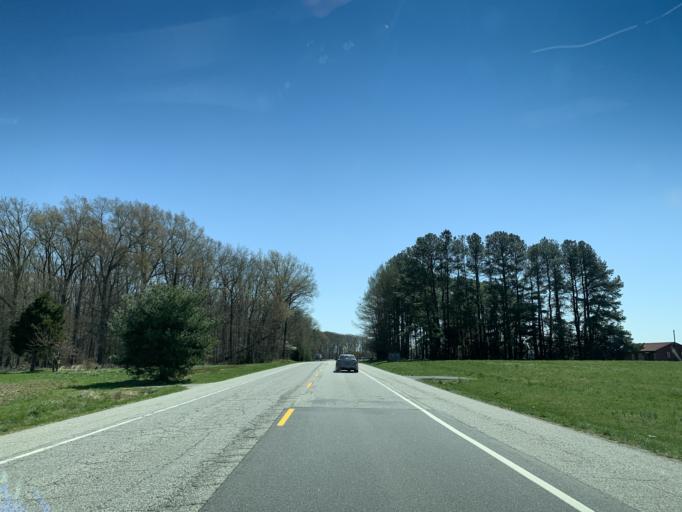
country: US
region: Maryland
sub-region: Caroline County
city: Ridgely
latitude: 38.9409
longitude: -75.9742
